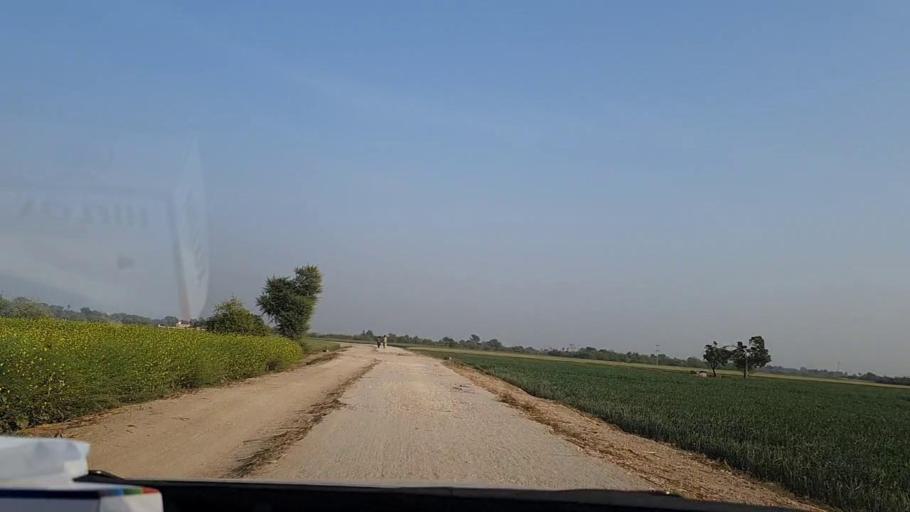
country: PK
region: Sindh
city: Tando Ghulam Ali
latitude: 25.2099
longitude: 68.8952
